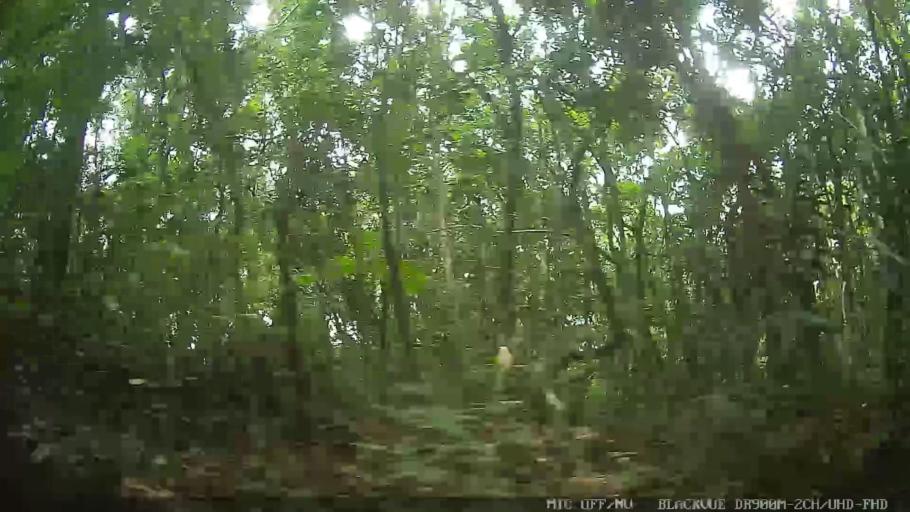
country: BR
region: Sao Paulo
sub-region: Mogi das Cruzes
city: Mogi das Cruzes
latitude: -23.5002
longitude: -46.2036
